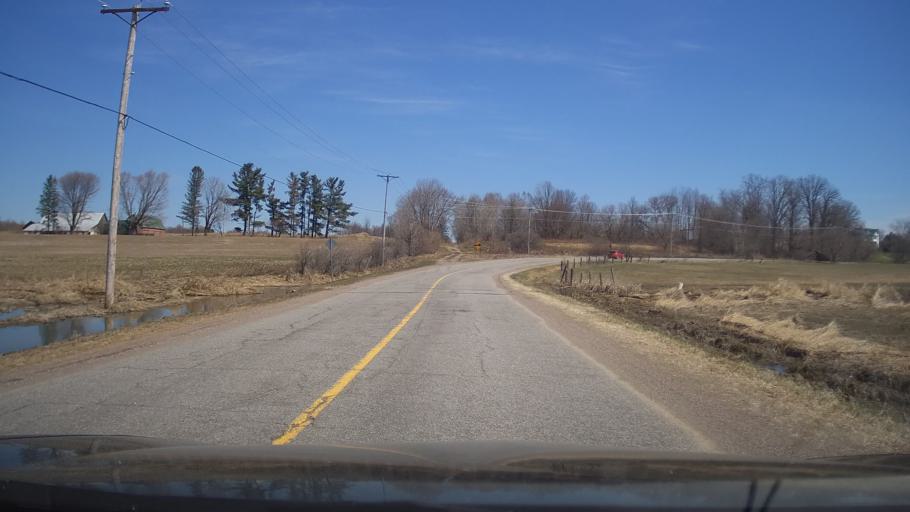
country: CA
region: Ontario
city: Arnprior
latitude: 45.5305
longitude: -76.3809
